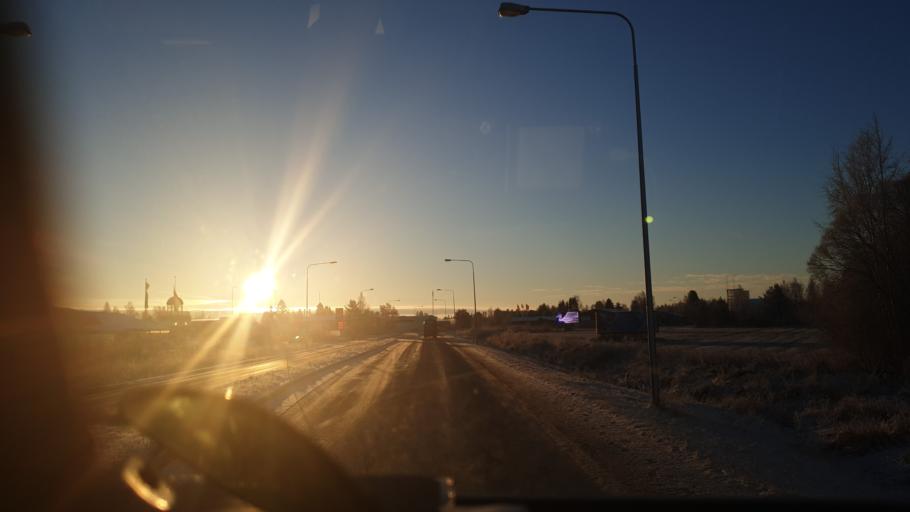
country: FI
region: Northern Ostrobothnia
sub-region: Ylivieska
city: Kalajoki
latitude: 64.2660
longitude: 23.9491
